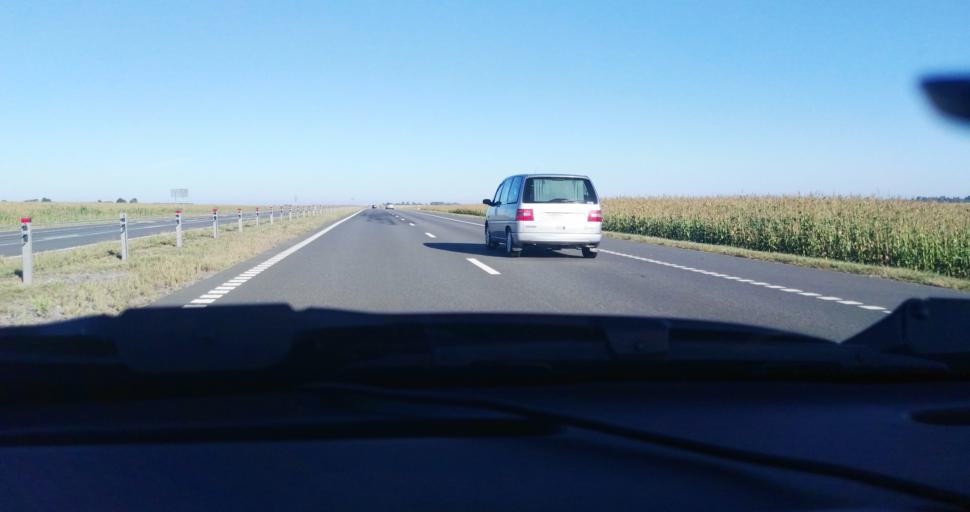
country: BY
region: Gomel
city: Buda-Kashalyova
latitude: 52.5243
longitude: 30.6192
